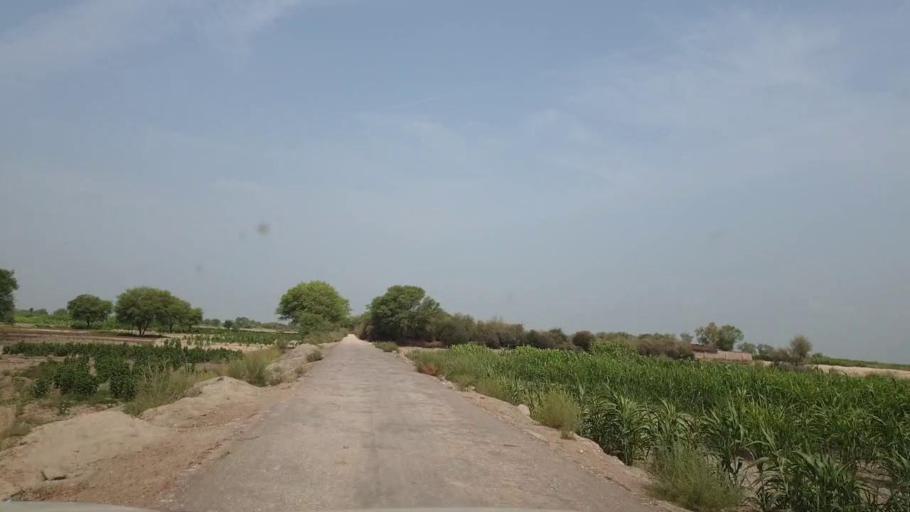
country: PK
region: Sindh
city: Sobhadero
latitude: 27.3947
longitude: 68.2621
